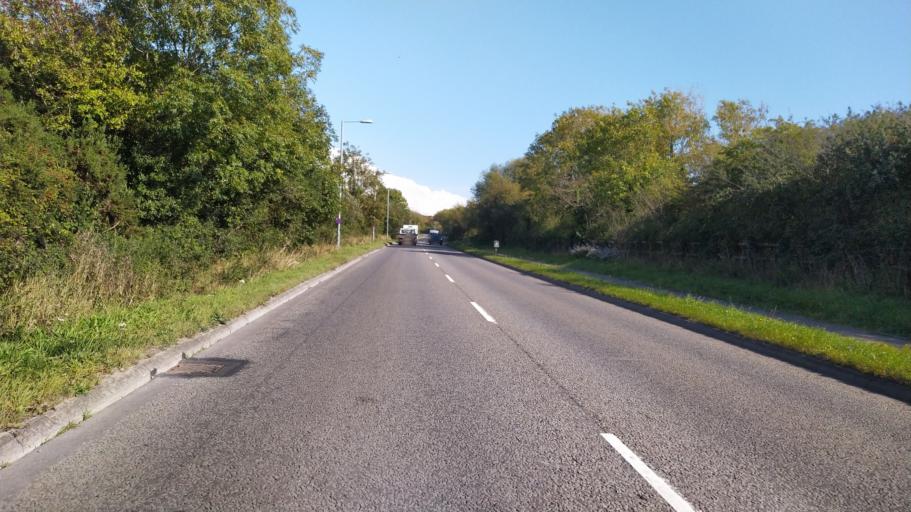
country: GB
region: England
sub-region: Dorset
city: Weymouth
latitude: 50.6193
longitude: -2.4761
